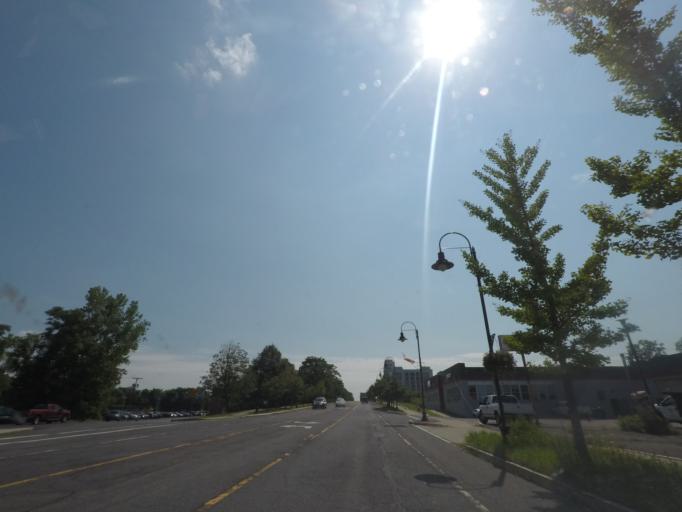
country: US
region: New York
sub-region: Albany County
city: Menands
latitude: 42.6900
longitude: -73.7262
